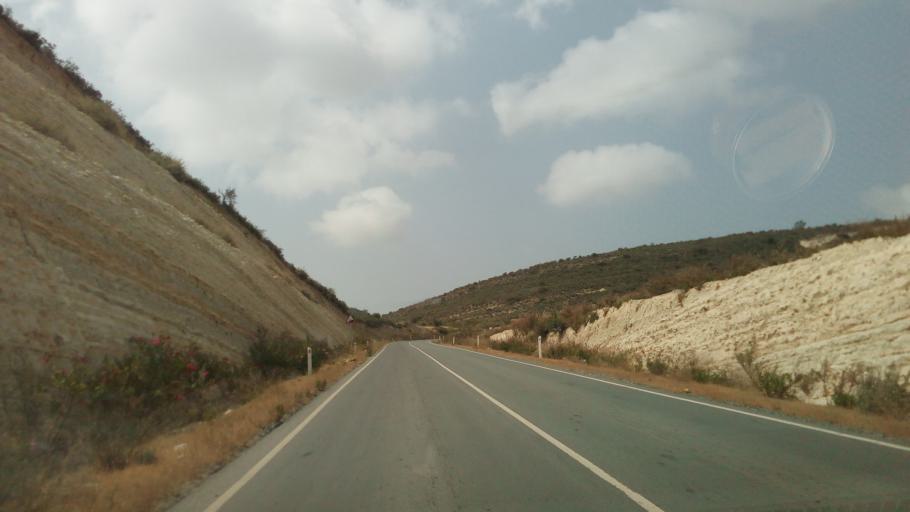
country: CY
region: Limassol
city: Pano Polemidia
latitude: 34.7454
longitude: 32.9541
